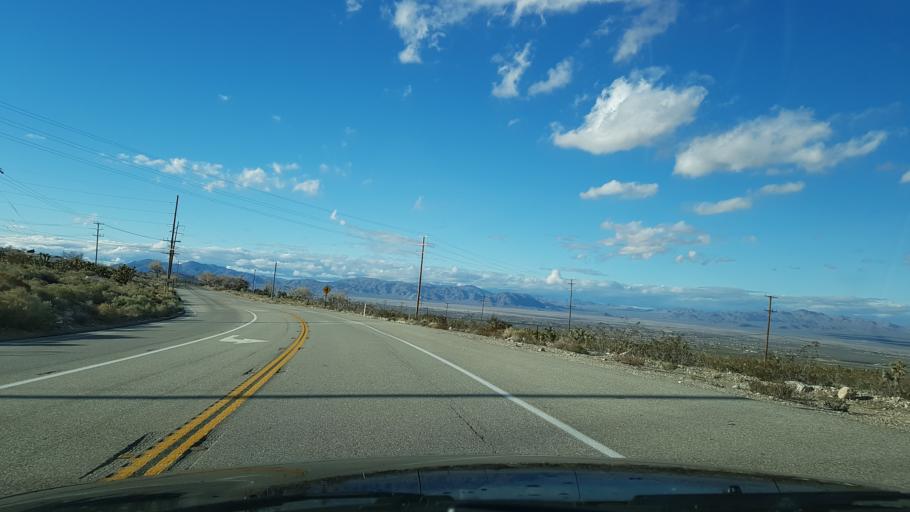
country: US
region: California
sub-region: San Bernardino County
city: Big Bear City
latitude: 34.3732
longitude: -116.8604
